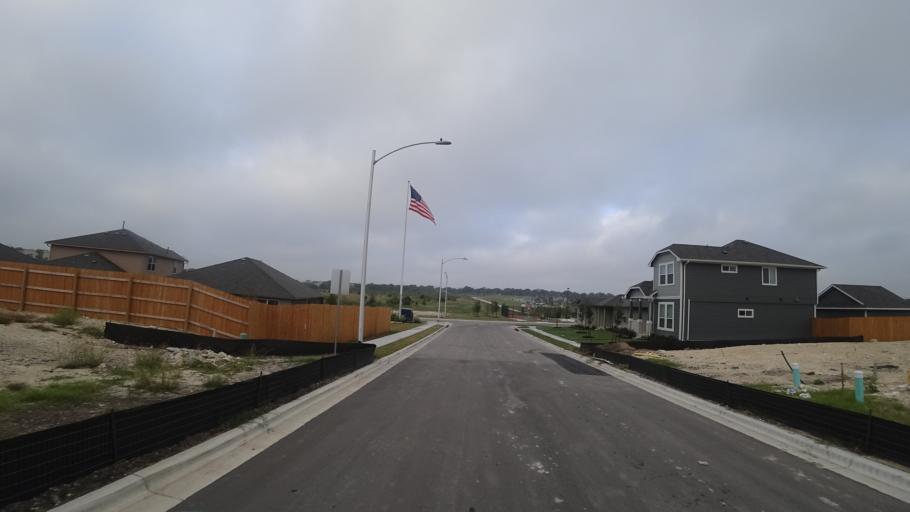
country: US
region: Texas
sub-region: Travis County
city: Wells Branch
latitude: 30.3577
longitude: -97.6648
